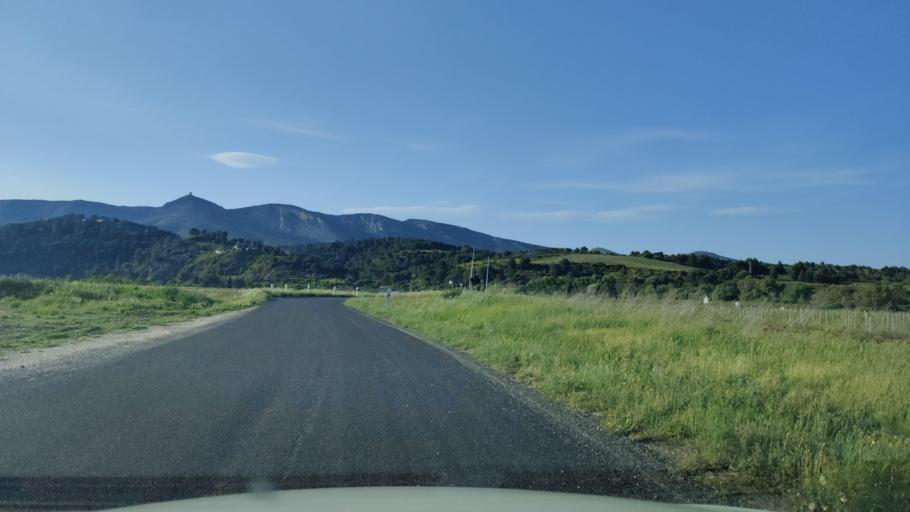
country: FR
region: Languedoc-Roussillon
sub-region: Departement des Pyrenees-Orientales
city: Baixas
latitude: 42.7790
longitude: 2.7776
